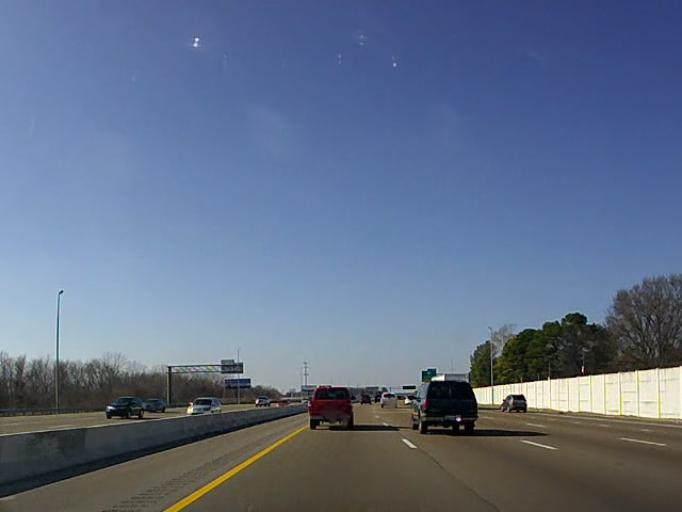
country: US
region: Tennessee
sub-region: Shelby County
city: Germantown
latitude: 35.0782
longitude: -89.9188
